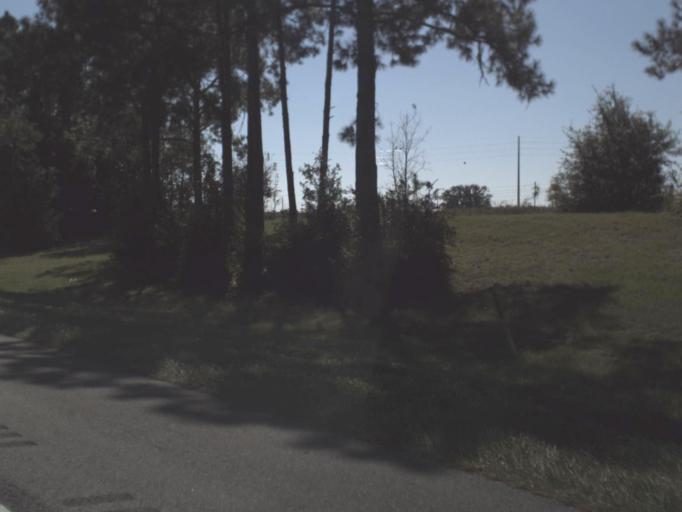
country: US
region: Florida
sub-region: Sumter County
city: Wildwood
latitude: 28.8025
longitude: -82.0023
